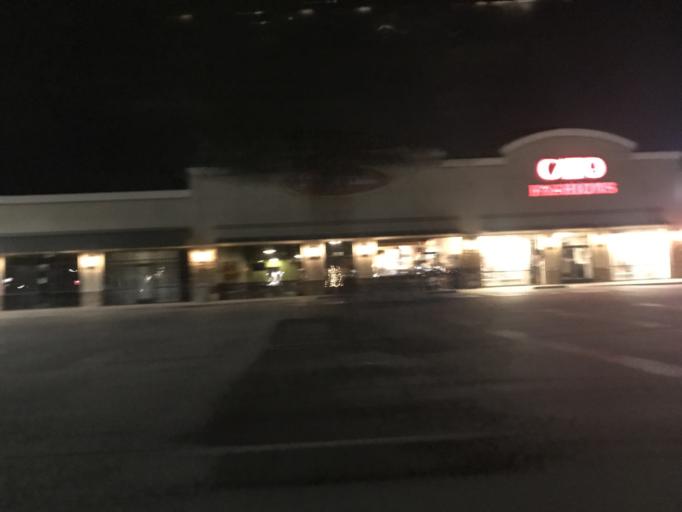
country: US
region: Texas
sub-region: Taylor County
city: Abilene
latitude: 32.4807
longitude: -99.6962
